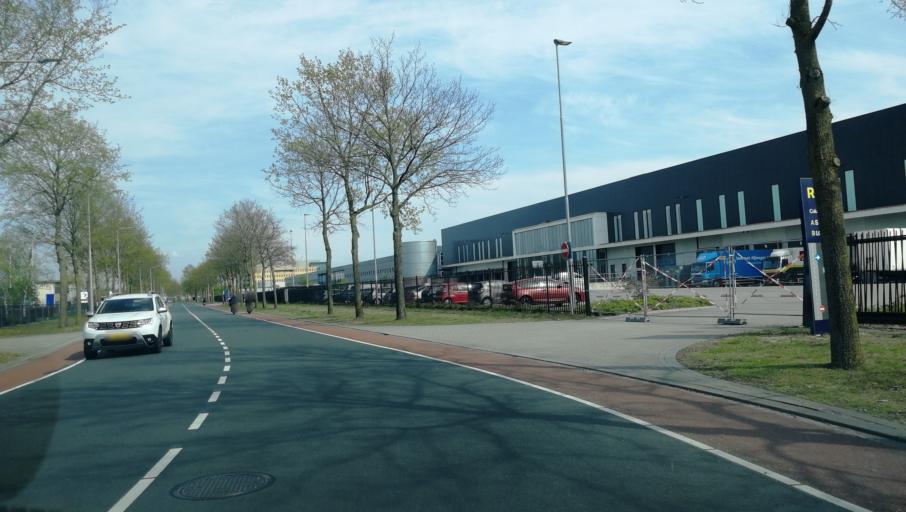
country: NL
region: Limburg
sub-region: Gemeente Peel en Maas
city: Maasbree
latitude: 51.3964
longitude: 6.0914
